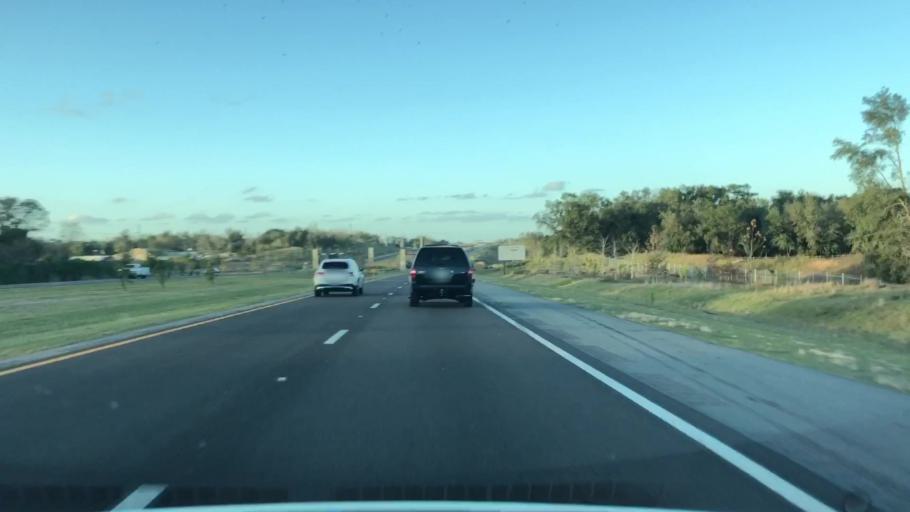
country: US
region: Florida
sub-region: Orange County
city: Zellwood
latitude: 28.7184
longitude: -81.5621
